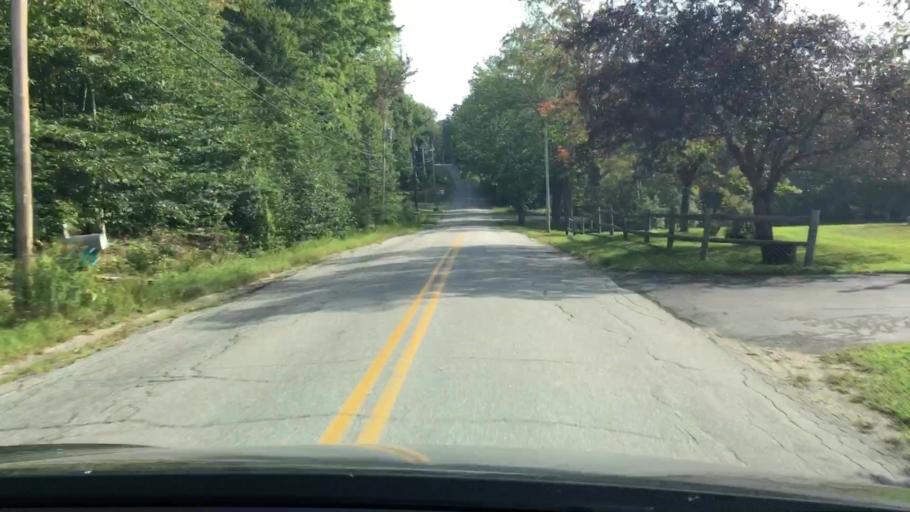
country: US
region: Maine
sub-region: Hancock County
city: Bucksport
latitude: 44.5531
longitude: -68.7958
